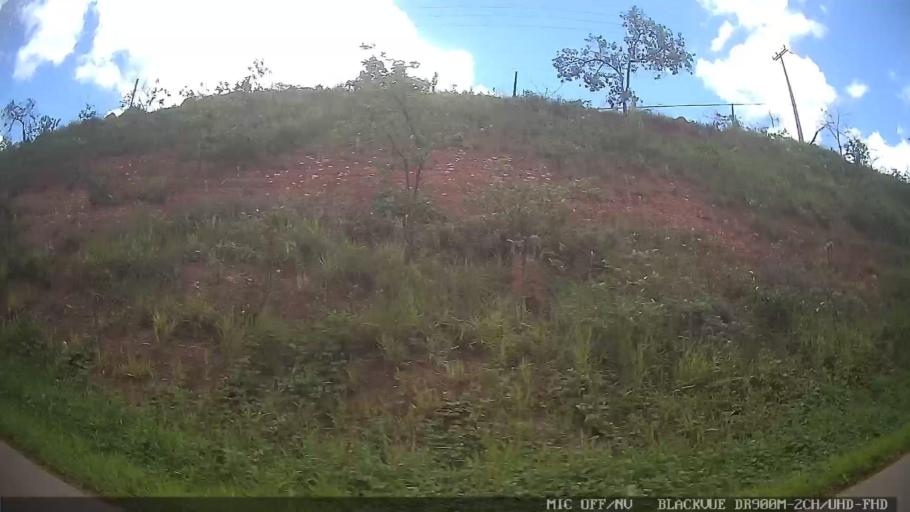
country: BR
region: Sao Paulo
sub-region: Amparo
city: Amparo
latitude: -22.8221
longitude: -46.6814
